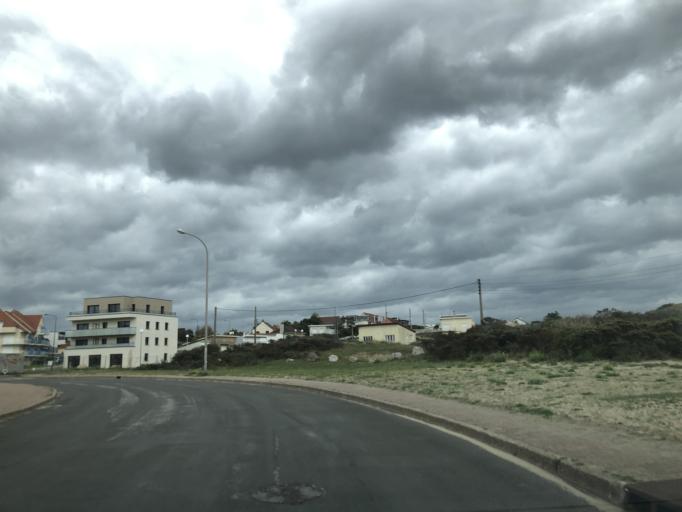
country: FR
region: Nord-Pas-de-Calais
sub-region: Departement du Pas-de-Calais
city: Cucq
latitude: 50.4793
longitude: 1.5779
